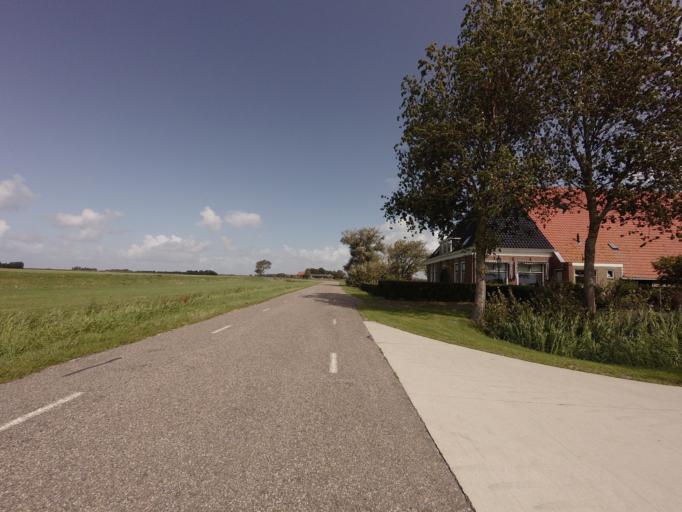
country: NL
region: Friesland
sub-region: Sudwest Fryslan
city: Makkum
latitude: 53.1049
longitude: 5.4315
